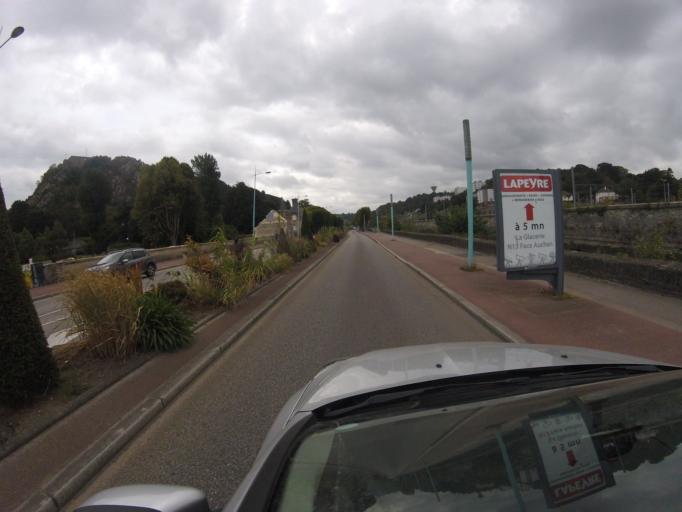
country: FR
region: Lower Normandy
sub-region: Departement de la Manche
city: Cherbourg-Octeville
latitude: 49.6331
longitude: -1.6175
